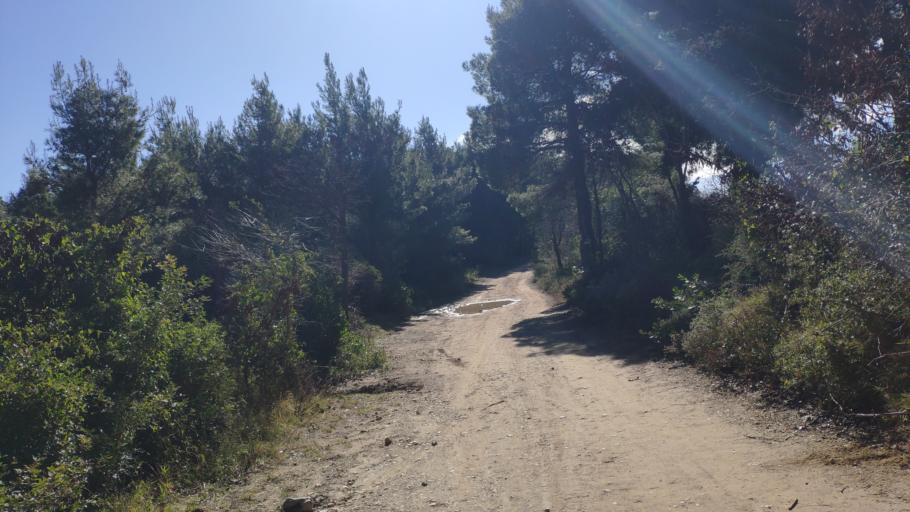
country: GR
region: Attica
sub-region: Nomarchia Anatolikis Attikis
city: Varybobi
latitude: 38.1546
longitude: 23.7765
